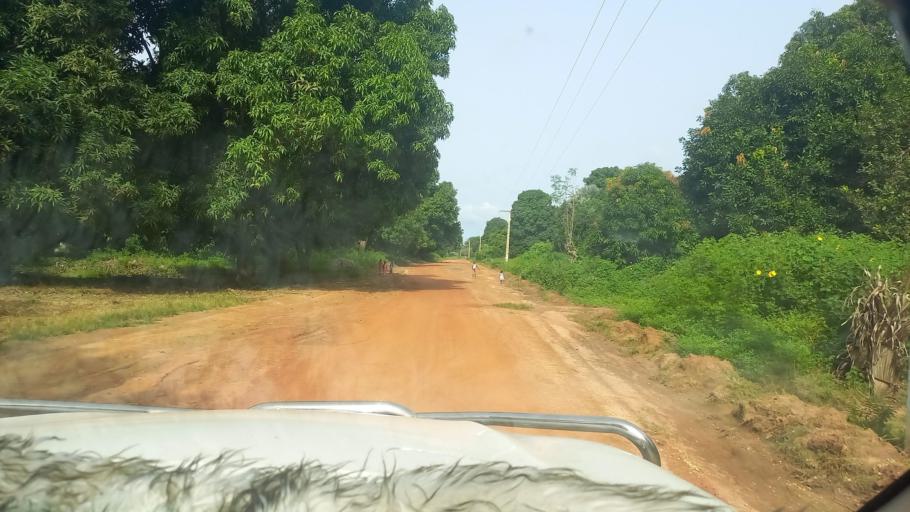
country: SN
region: Ziguinchor
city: Ziguinchor
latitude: 12.6701
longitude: -16.2731
